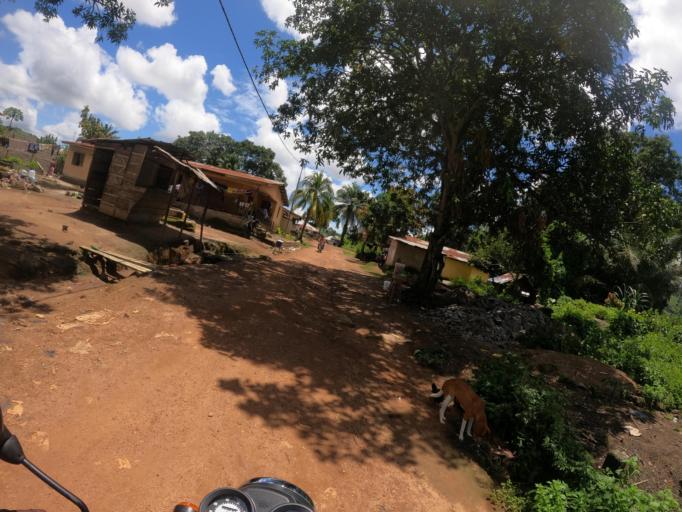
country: SL
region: Northern Province
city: Makeni
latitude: 8.8925
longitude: -12.0652
